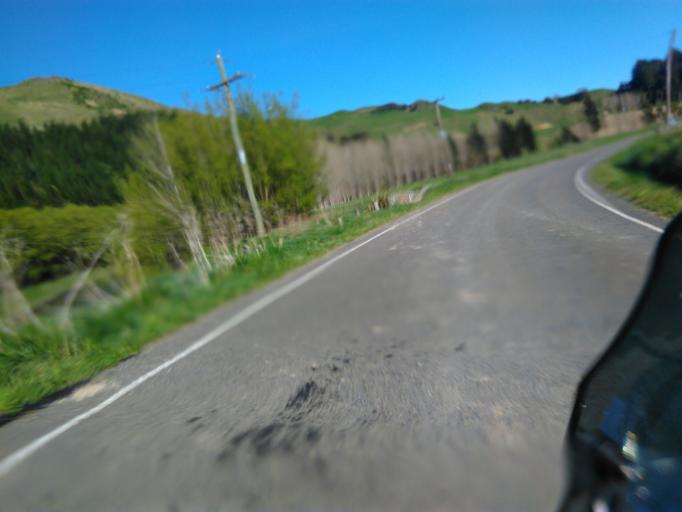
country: NZ
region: Gisborne
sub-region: Gisborne District
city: Gisborne
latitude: -38.4376
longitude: 177.7452
